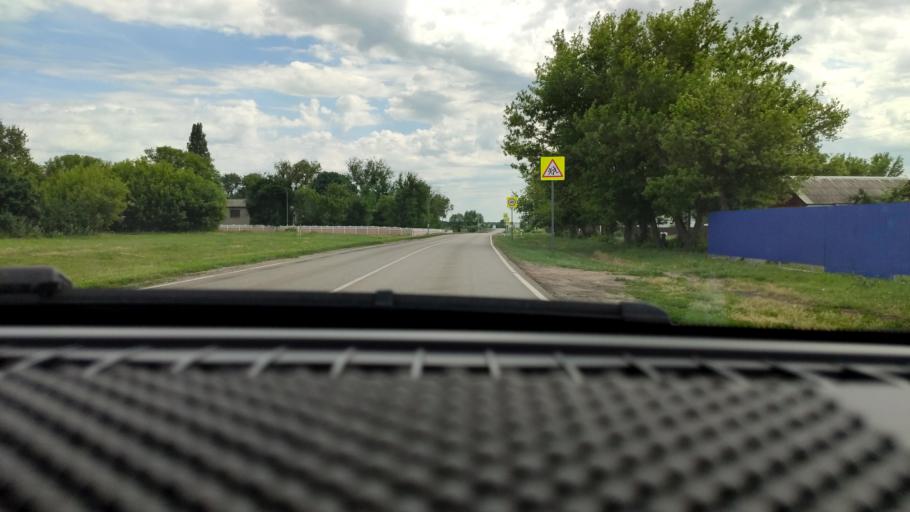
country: RU
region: Voronezj
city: Verkhnyaya Khava
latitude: 51.6794
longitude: 39.9415
